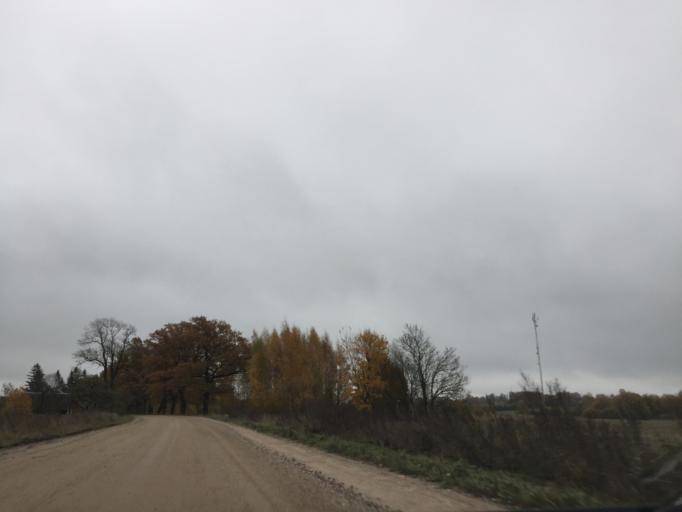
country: LV
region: Sigulda
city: Sigulda
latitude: 57.2674
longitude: 24.8653
